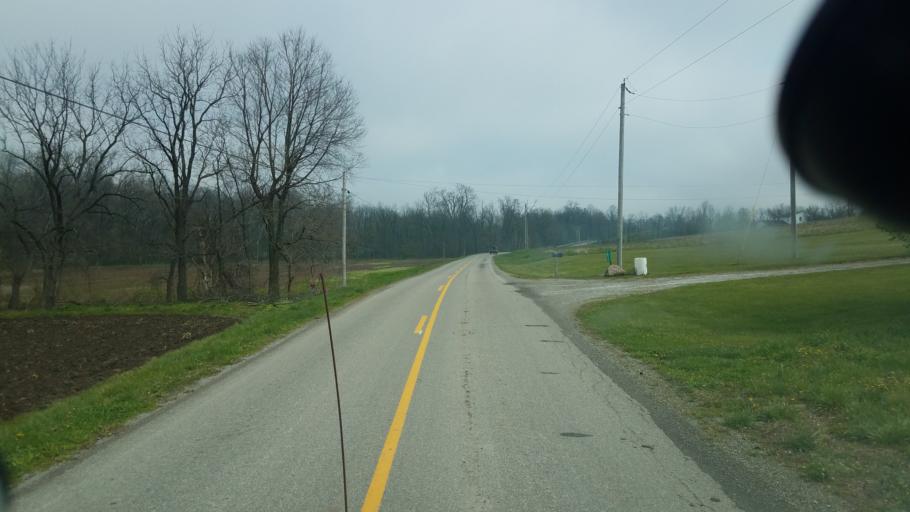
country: US
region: Ohio
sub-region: Hardin County
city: Kenton
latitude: 40.5767
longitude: -83.6315
